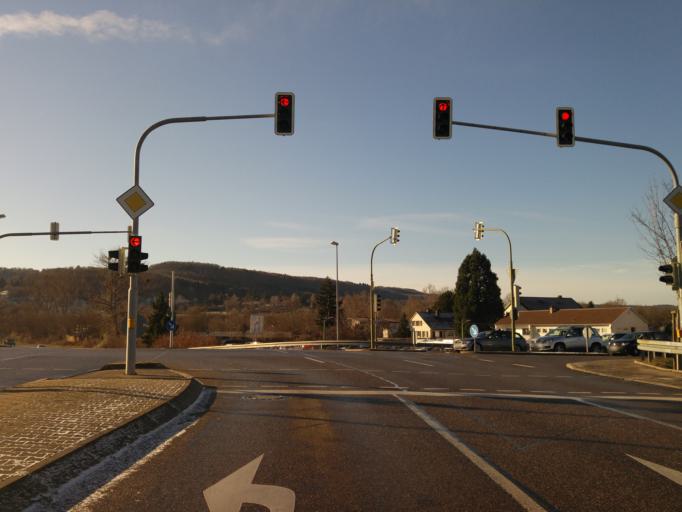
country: DE
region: Baden-Wuerttemberg
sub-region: Regierungsbezirk Stuttgart
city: Leonberg
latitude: 48.7872
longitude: 9.0159
